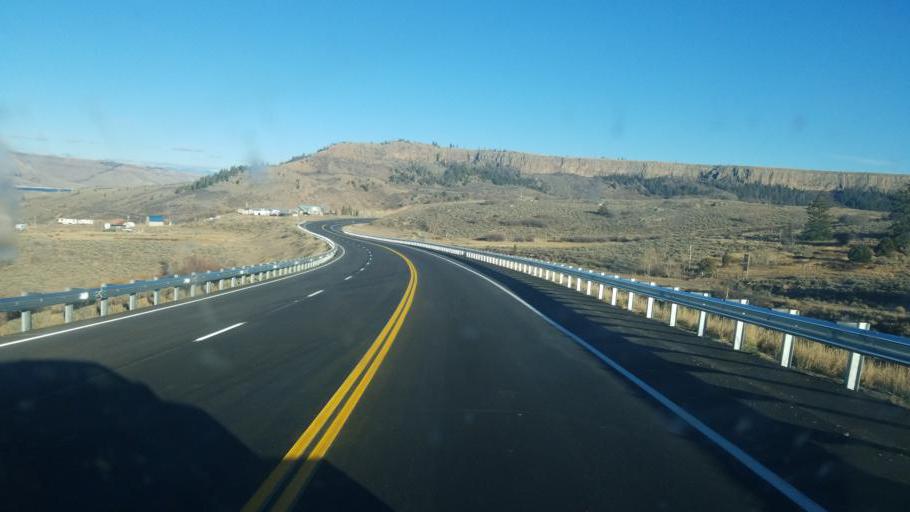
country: US
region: Colorado
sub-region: Hinsdale County
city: Lake City
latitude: 38.4405
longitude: -107.3544
